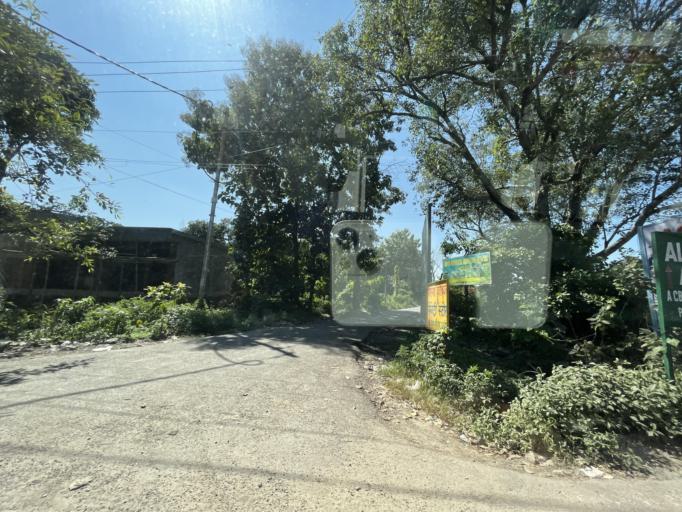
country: IN
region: Uttarakhand
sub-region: Naini Tal
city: Haldwani
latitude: 29.2135
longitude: 79.4553
